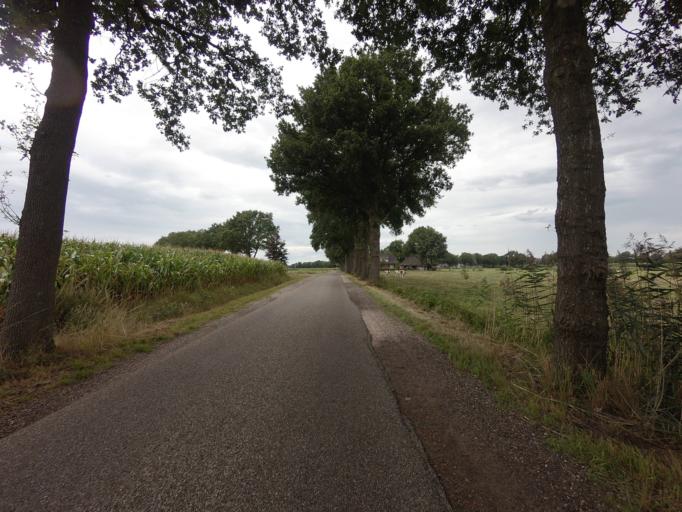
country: NL
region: Overijssel
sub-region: Gemeente Raalte
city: Raalte
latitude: 52.3620
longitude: 6.3533
